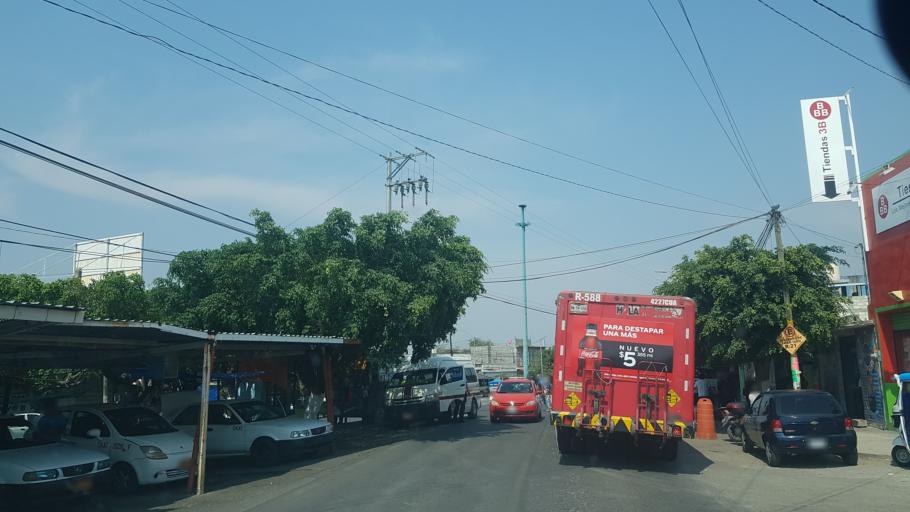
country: MX
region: Morelos
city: Amayuca
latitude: 18.7229
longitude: -98.7941
